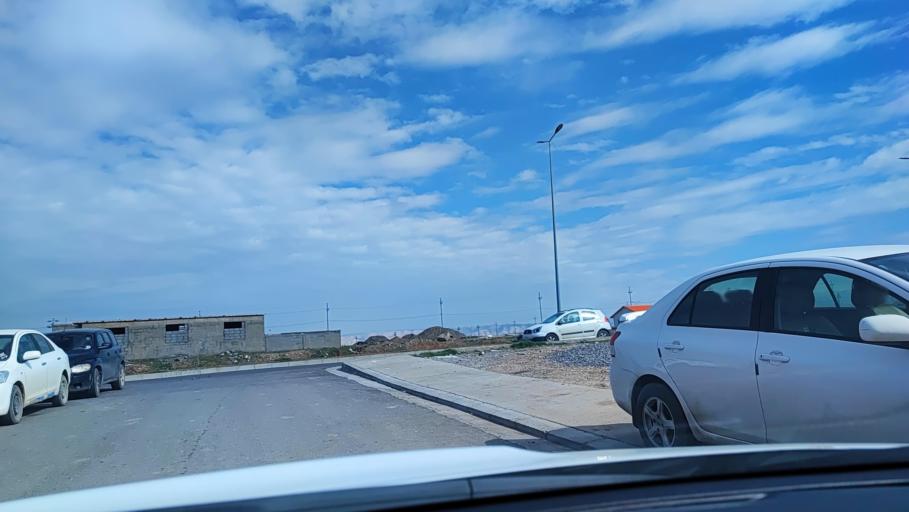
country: IQ
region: Arbil
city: Erbil
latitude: 36.2855
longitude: 44.0705
